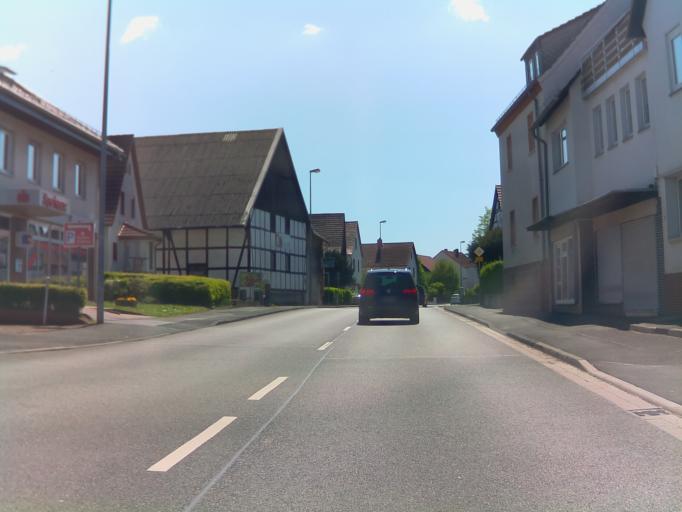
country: DE
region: Hesse
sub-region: Regierungsbezirk Kassel
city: Bad Hersfeld
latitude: 50.8328
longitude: 9.6669
